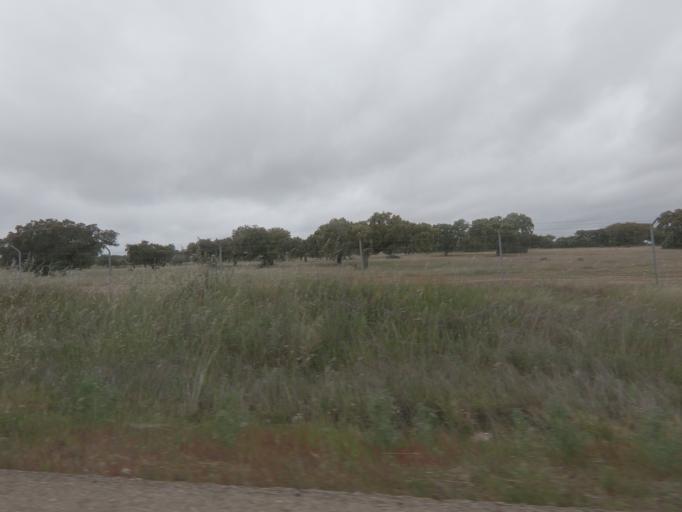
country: ES
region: Extremadura
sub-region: Provincia de Badajoz
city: Villar del Rey
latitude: 39.0071
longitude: -6.8596
